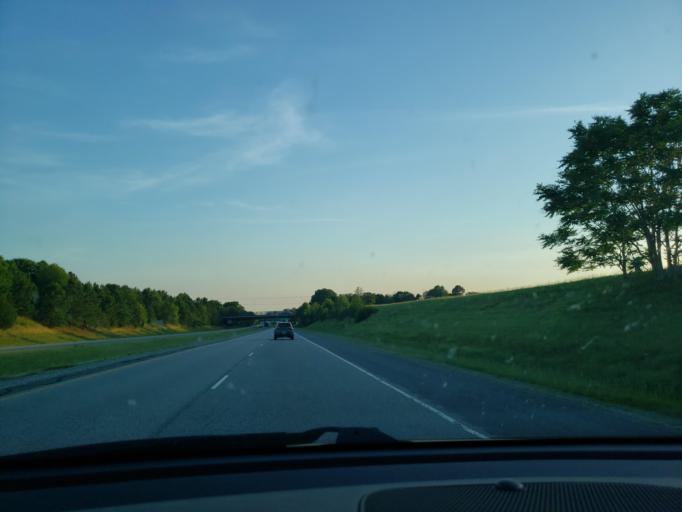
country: US
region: Virginia
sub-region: Henrico County
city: Fort Lee
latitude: 37.4637
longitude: -77.3757
